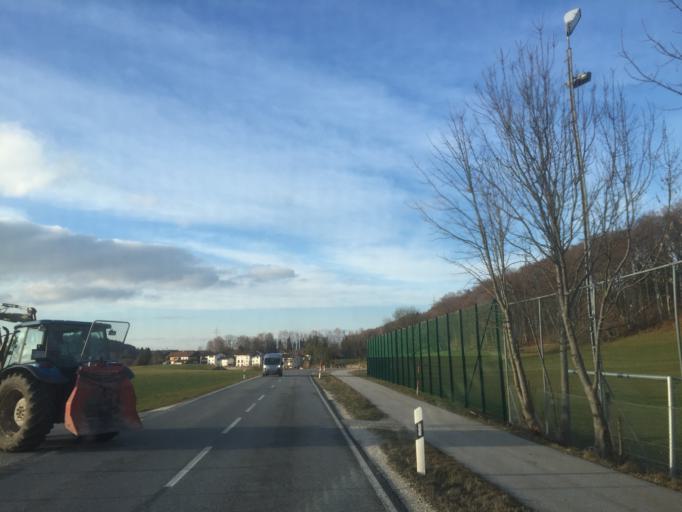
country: DE
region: Bavaria
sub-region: Upper Bavaria
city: Vachendorf
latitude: 47.8474
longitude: 12.6015
